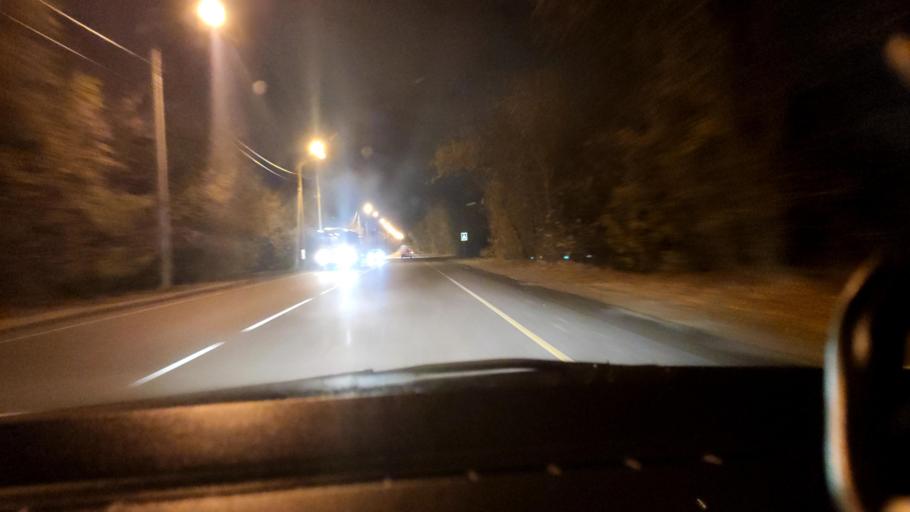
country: RU
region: Voronezj
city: Voronezh
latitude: 51.6016
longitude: 39.1775
